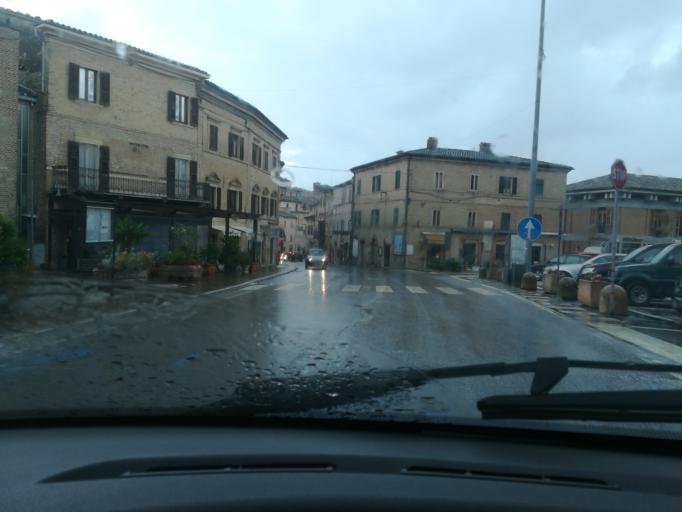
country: IT
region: The Marches
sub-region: Provincia di Macerata
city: Sarnano
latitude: 43.0357
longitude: 13.2984
